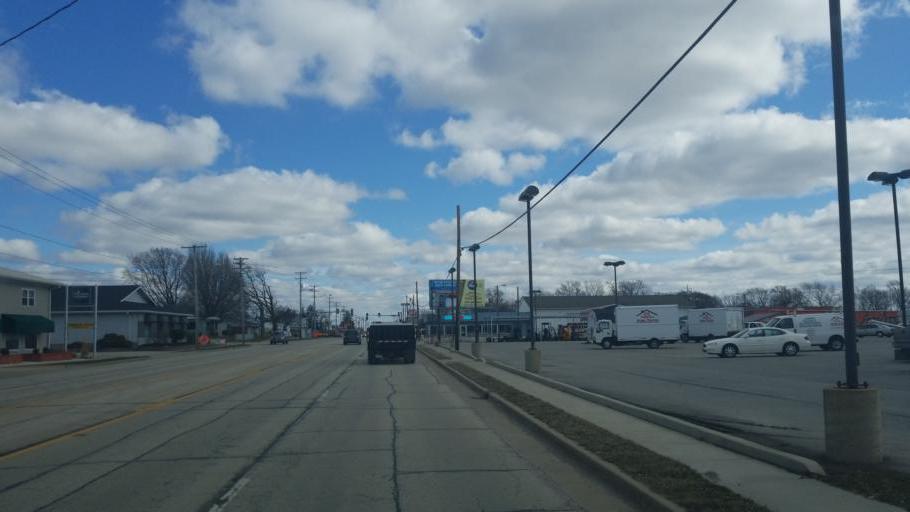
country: US
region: Illinois
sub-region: Douglas County
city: Tuscola
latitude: 39.7916
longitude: -88.2817
